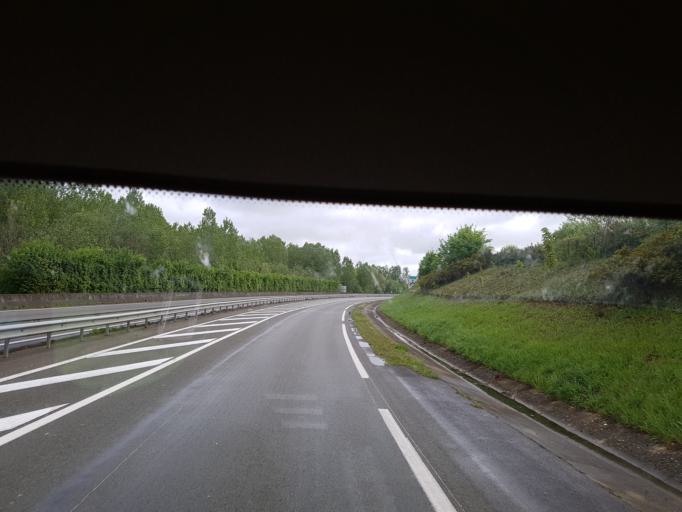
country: FR
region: Picardie
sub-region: Departement de l'Aisne
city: Courmelles
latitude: 49.3574
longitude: 3.3114
